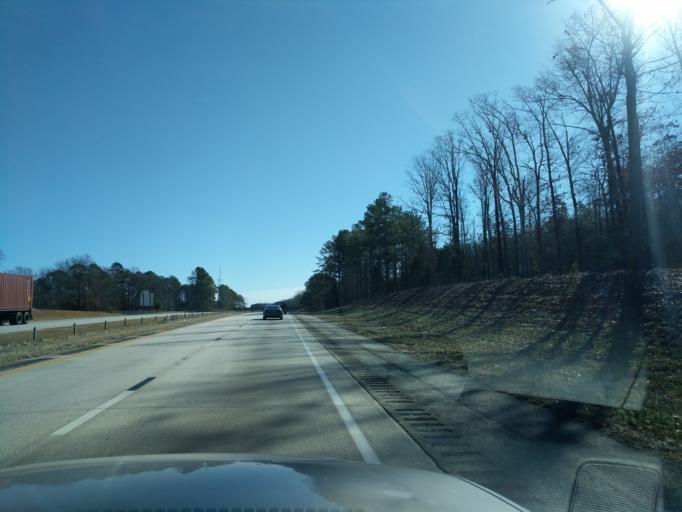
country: US
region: South Carolina
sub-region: Laurens County
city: Watts Mills
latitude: 34.5485
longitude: -81.9856
